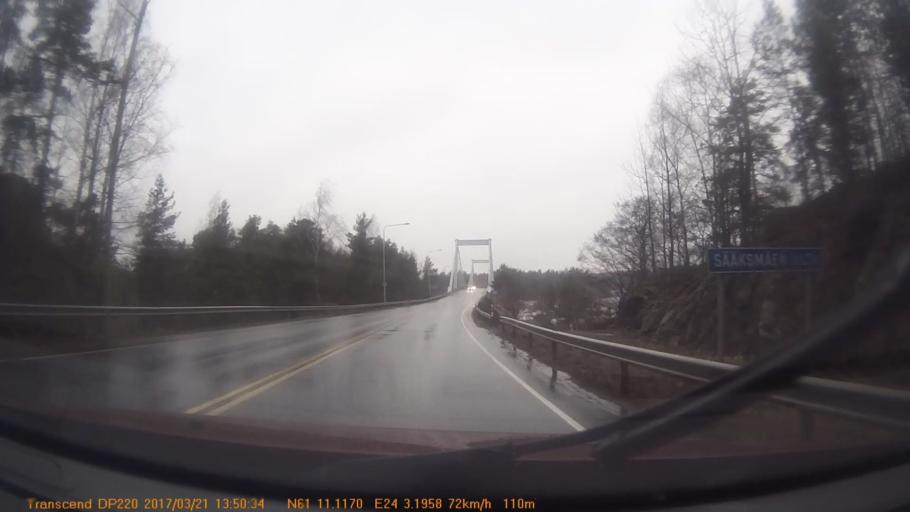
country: FI
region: Pirkanmaa
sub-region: Etelae-Pirkanmaa
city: Valkeakoski
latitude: 61.1855
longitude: 24.0539
